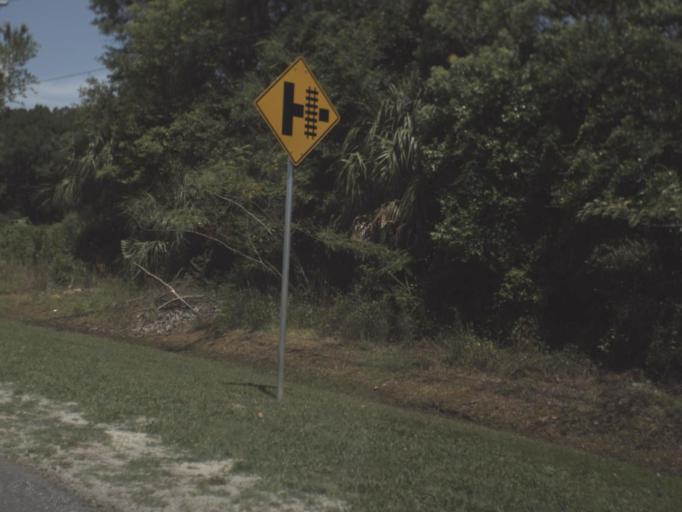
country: US
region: Florida
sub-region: Suwannee County
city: Live Oak
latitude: 30.3010
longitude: -82.9945
